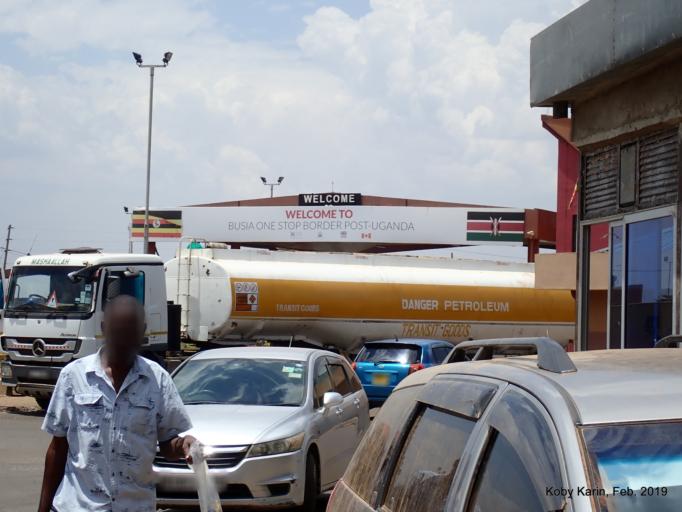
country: UG
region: Eastern Region
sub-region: Busia District
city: Busia
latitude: 0.4652
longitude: 34.0991
